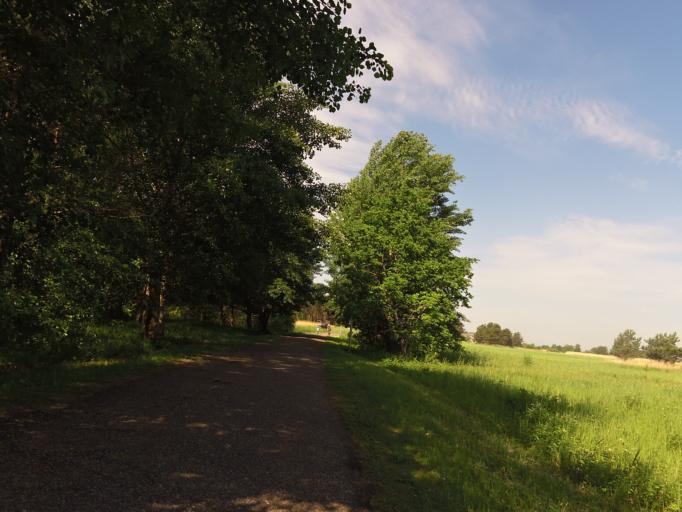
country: EE
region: Laeaene
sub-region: Haapsalu linn
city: Haapsalu
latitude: 58.9391
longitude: 23.5260
